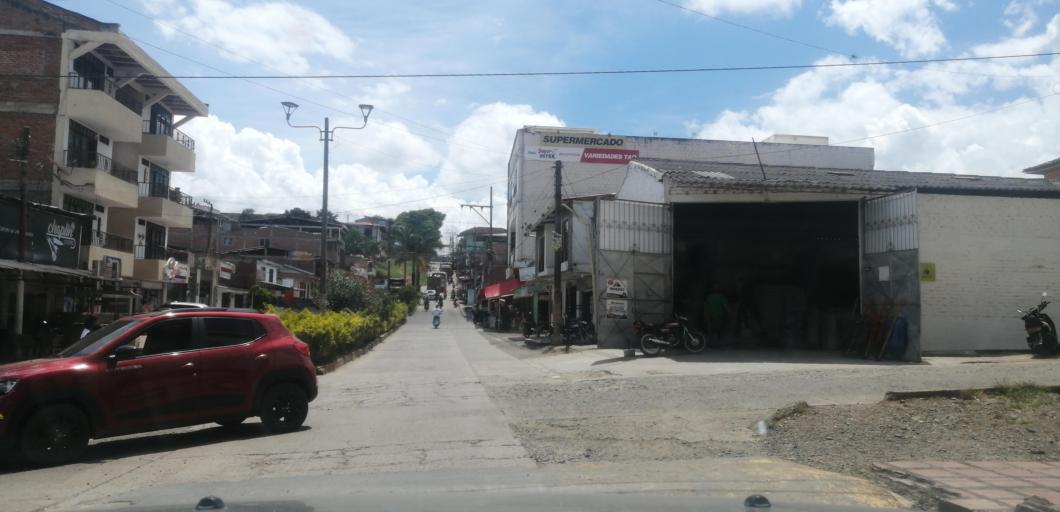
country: CO
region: Valle del Cauca
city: Restrepo
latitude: 3.8227
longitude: -76.5224
